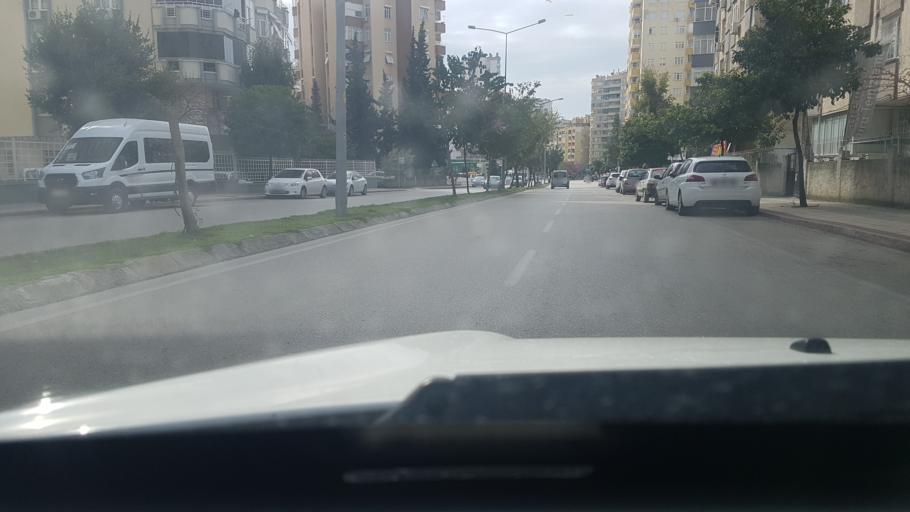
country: TR
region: Adana
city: Adana
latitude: 37.0421
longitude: 35.3016
